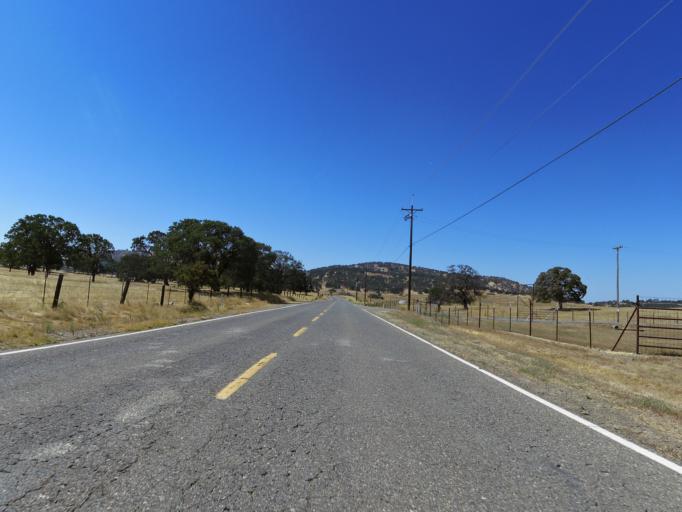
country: US
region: California
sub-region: Tuolumne County
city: Tuolumne City
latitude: 37.6502
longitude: -120.3113
